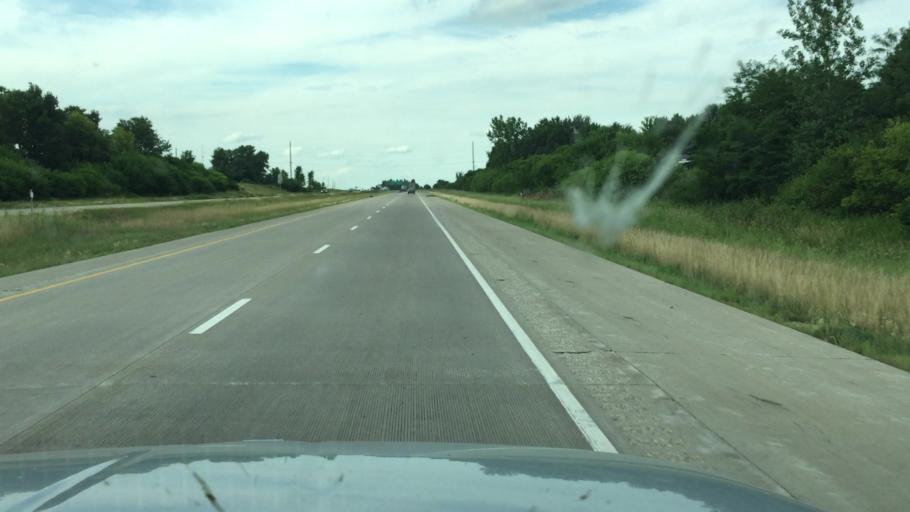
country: US
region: Iowa
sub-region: Scott County
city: Walcott
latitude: 41.5780
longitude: -90.6769
